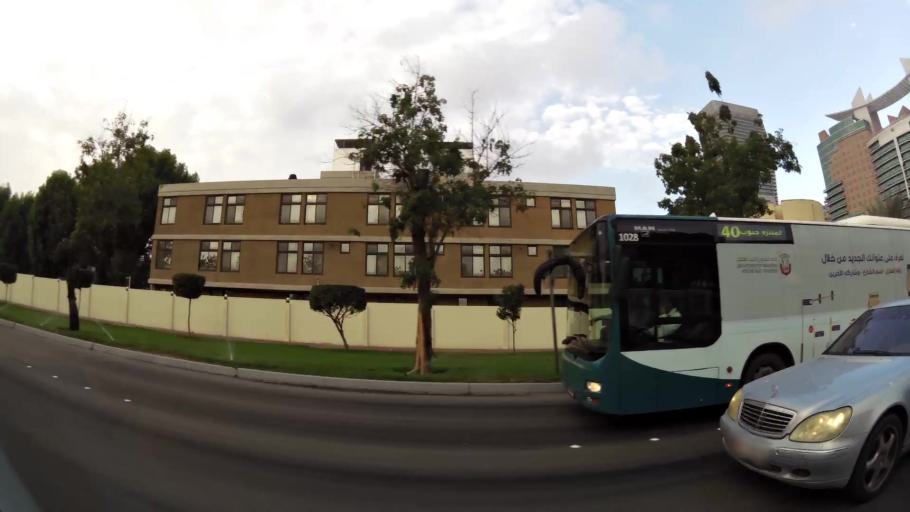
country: AE
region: Abu Dhabi
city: Abu Dhabi
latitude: 24.4686
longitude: 54.3430
